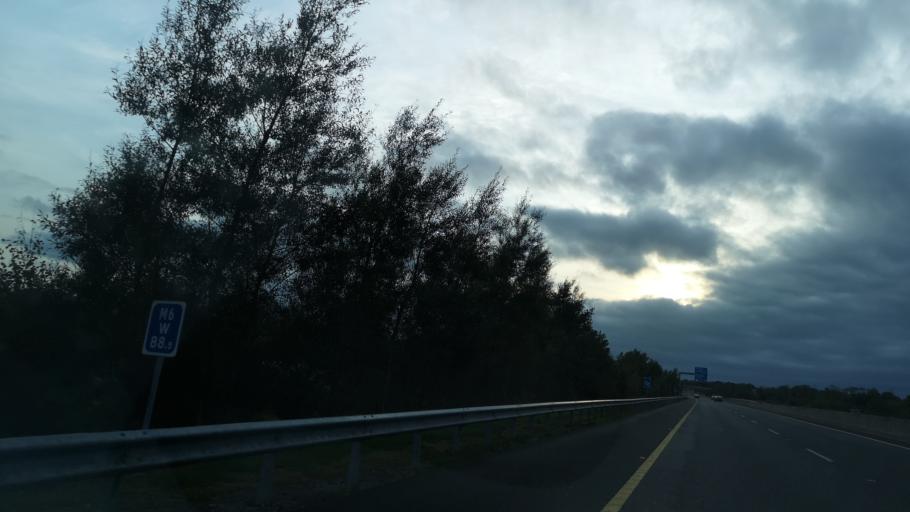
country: IE
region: Connaught
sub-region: County Galway
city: Ballinasloe
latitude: 53.3174
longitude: -8.2282
